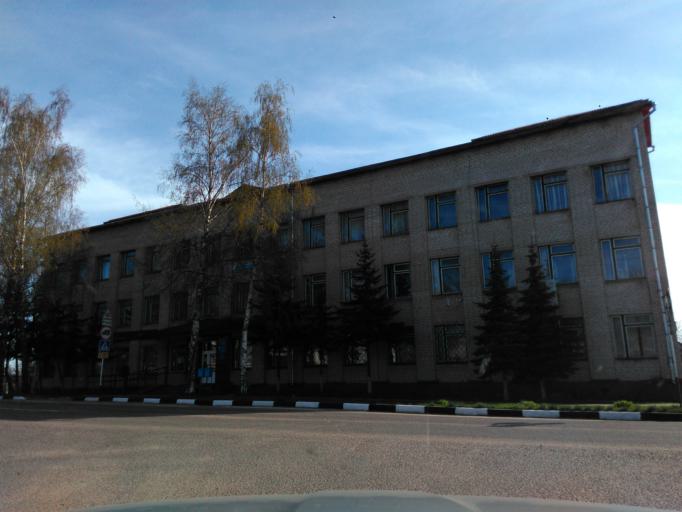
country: BY
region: Vitebsk
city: Chashniki
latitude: 54.8599
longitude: 29.1635
